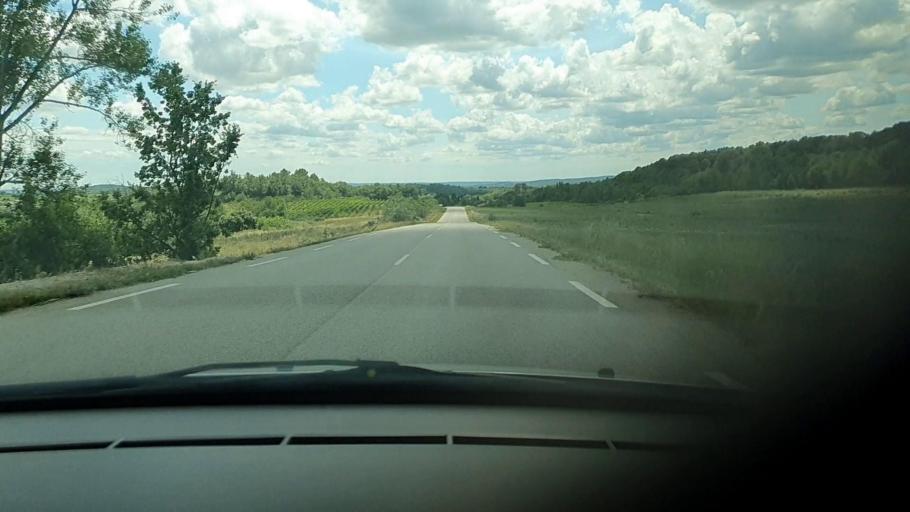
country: FR
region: Languedoc-Roussillon
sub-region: Departement du Gard
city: Moussac
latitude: 44.0430
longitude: 4.2328
